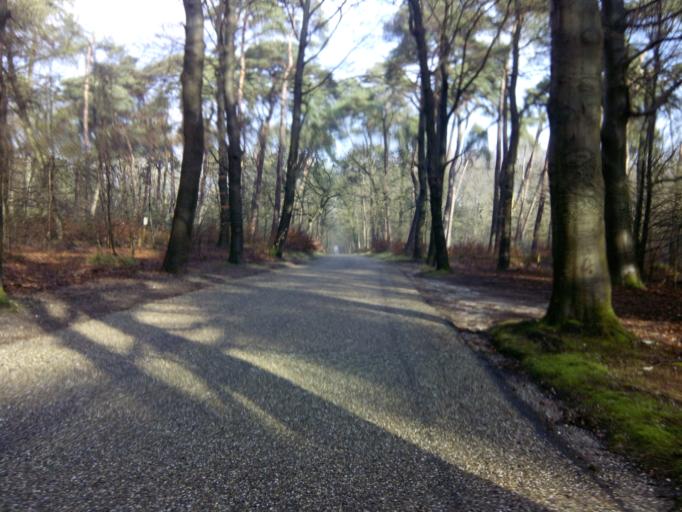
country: NL
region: Utrecht
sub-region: Gemeente Utrechtse Heuvelrug
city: Maarsbergen
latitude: 52.0375
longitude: 5.3973
